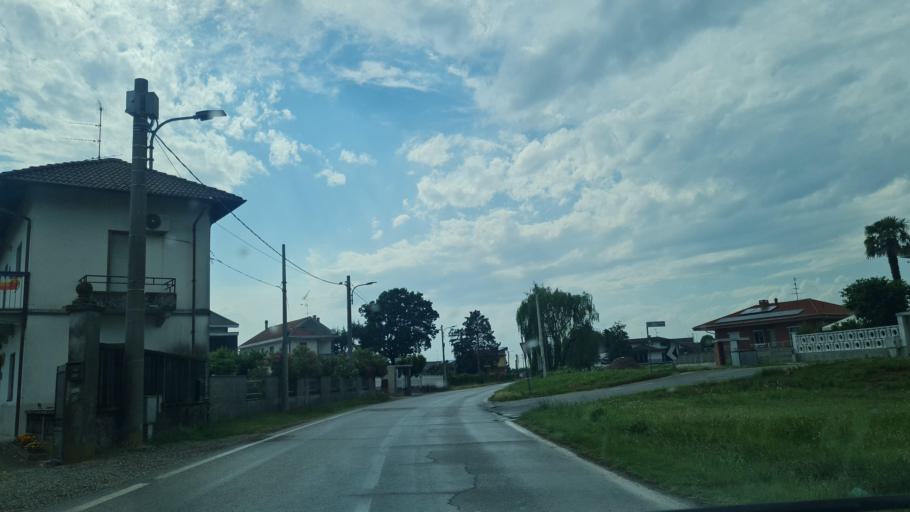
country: IT
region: Piedmont
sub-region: Provincia di Novara
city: Cameri
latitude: 45.5026
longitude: 8.6530
